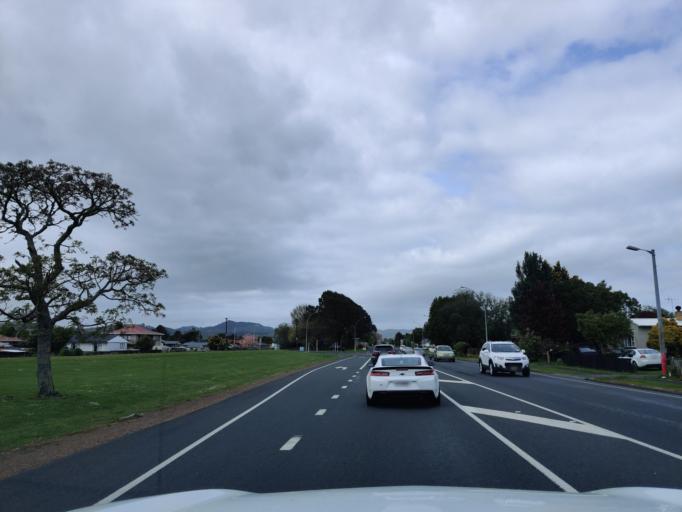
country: NZ
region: Waikato
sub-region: Waikato District
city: Ngaruawahia
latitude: -37.5377
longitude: 175.1585
